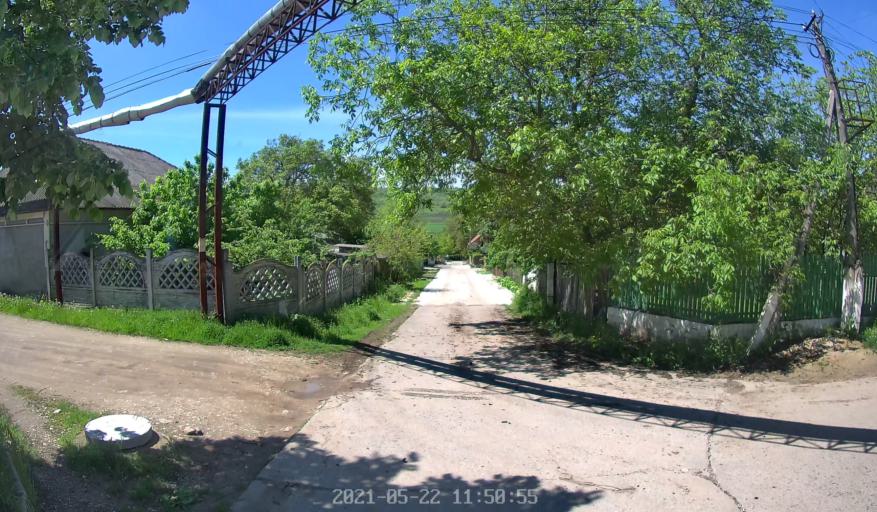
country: MD
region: Chisinau
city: Stauceni
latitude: 47.0973
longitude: 28.8282
